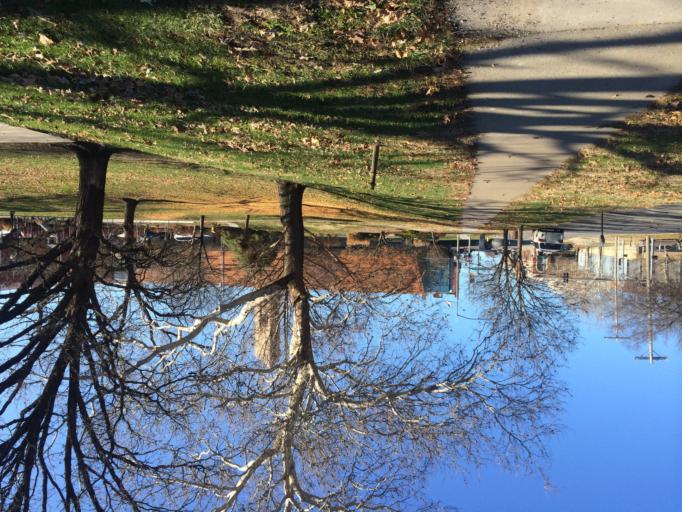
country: US
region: Kansas
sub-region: Douglas County
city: Lawrence
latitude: 38.9712
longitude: -95.2393
